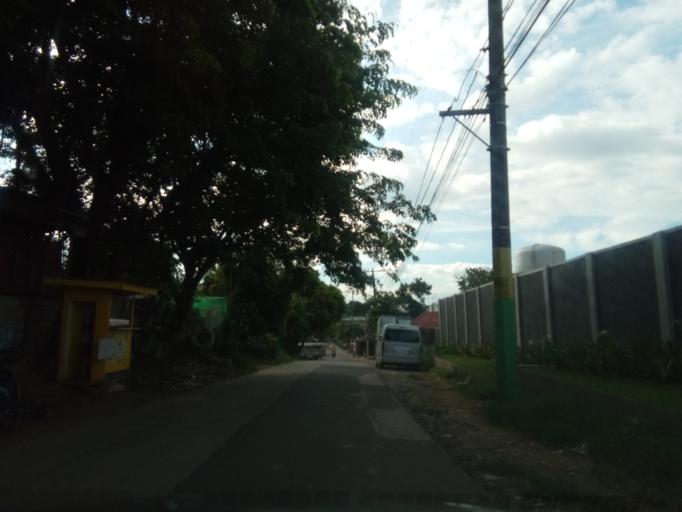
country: PH
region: Calabarzon
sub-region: Province of Cavite
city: Biga
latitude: 14.2816
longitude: 120.9464
